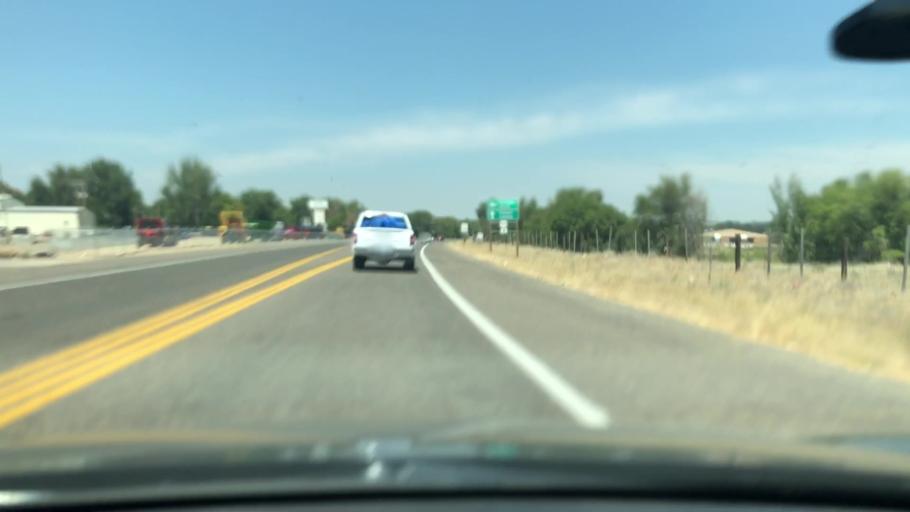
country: US
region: Idaho
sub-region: Owyhee County
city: Homedale
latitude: 43.6079
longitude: -116.9310
